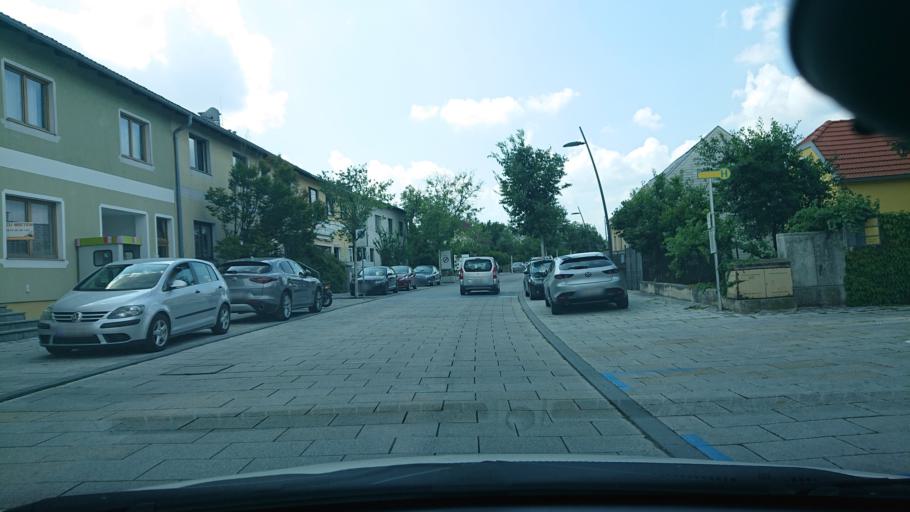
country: AT
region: Lower Austria
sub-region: Politischer Bezirk Baden
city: Kottingbrunn
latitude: 47.9491
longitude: 16.2247
